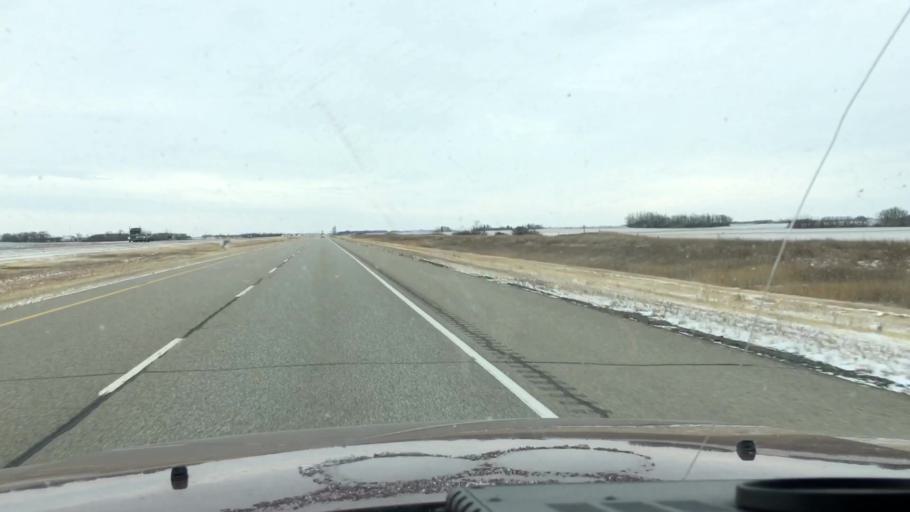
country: CA
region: Saskatchewan
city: Watrous
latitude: 51.3220
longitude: -106.0694
